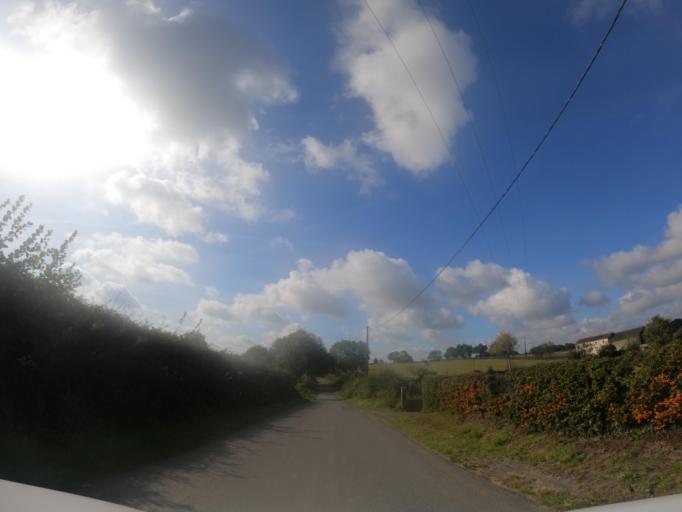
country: FR
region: Poitou-Charentes
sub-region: Departement des Deux-Sevres
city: Courlay
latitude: 46.7775
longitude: -0.5928
